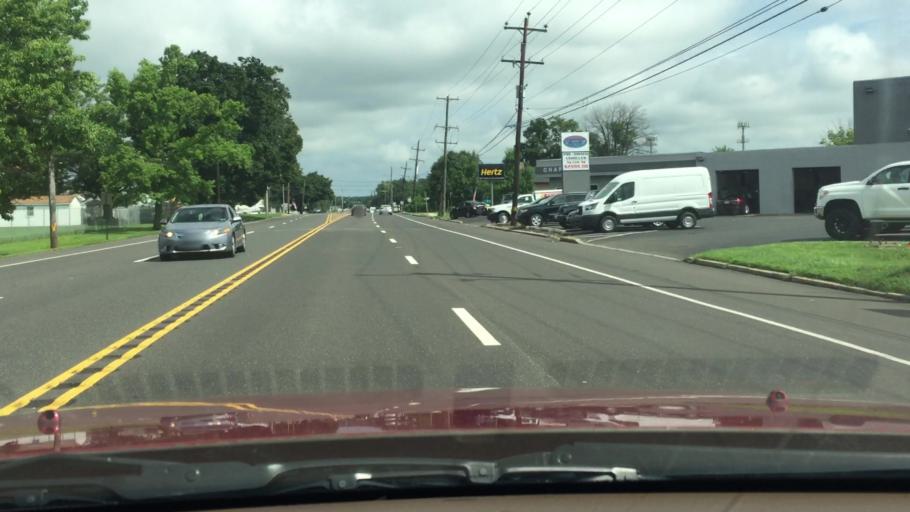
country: US
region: Pennsylvania
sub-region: Montgomery County
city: Horsham
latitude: 40.2003
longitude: -75.1390
